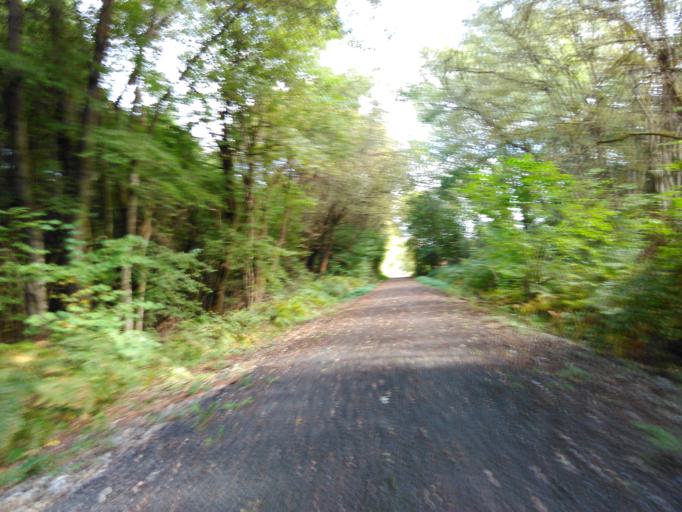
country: BE
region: Wallonia
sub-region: Province du Luxembourg
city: Vaux-sur-Sure
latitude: 49.9458
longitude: 5.5957
